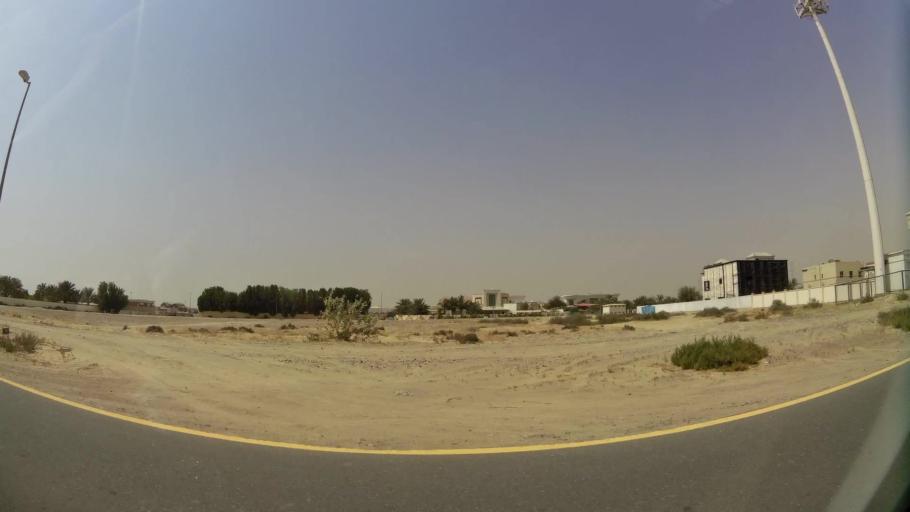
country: AE
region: Ash Shariqah
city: Sharjah
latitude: 25.2553
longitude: 55.4744
